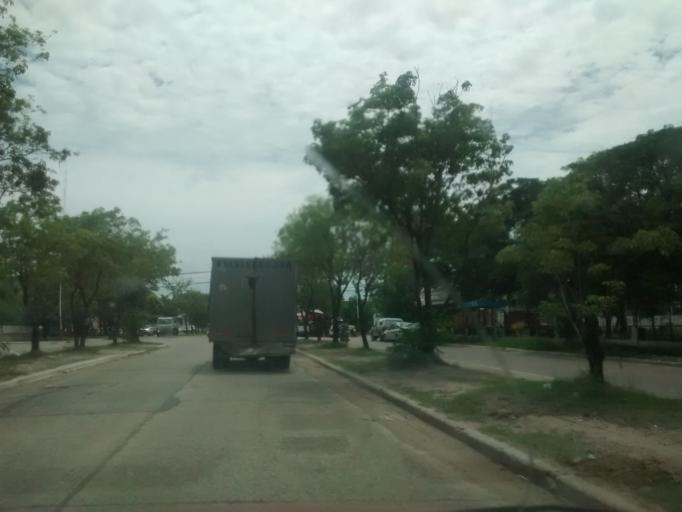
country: AR
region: Chaco
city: Resistencia
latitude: -27.4625
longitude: -58.9850
